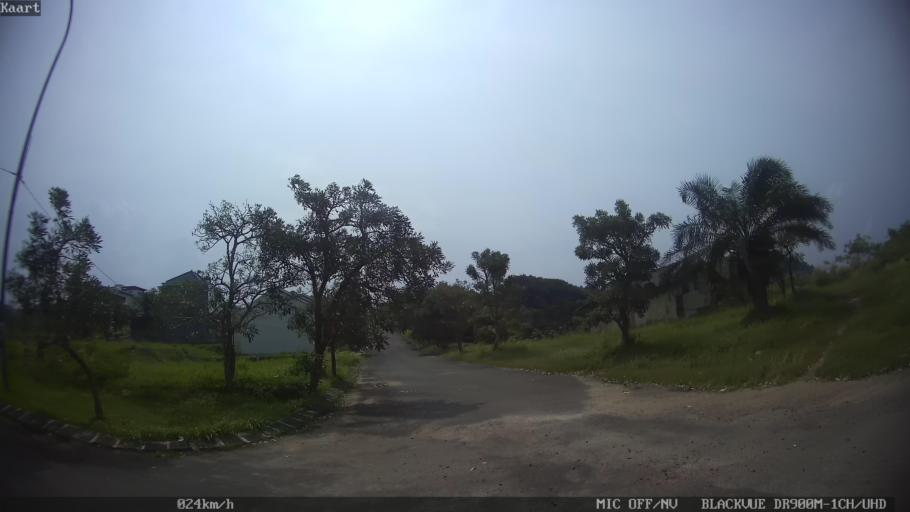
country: ID
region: Lampung
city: Bandarlampung
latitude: -5.4307
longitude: 105.2842
